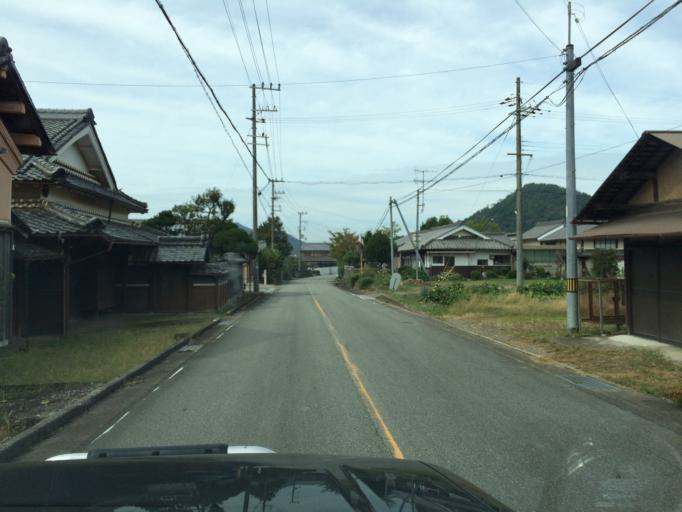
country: JP
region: Hyogo
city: Sasayama
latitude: 35.0693
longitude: 135.2990
